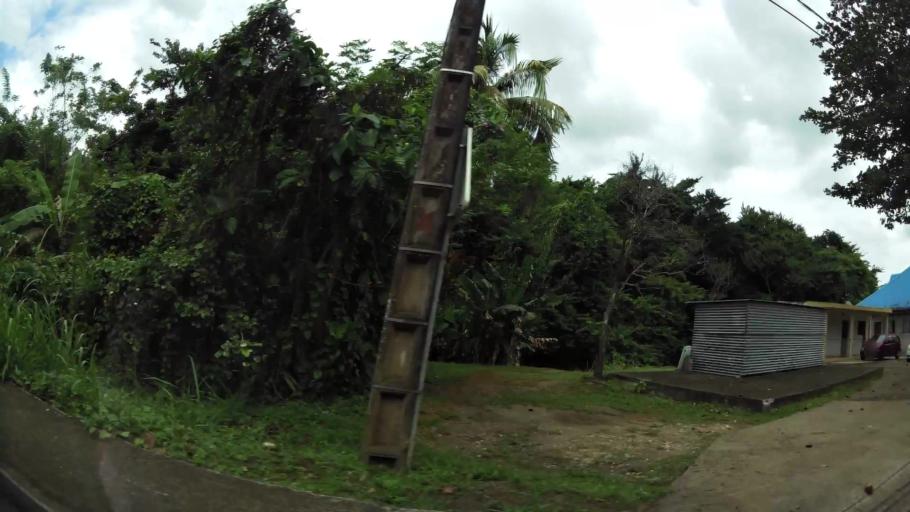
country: GP
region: Guadeloupe
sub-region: Guadeloupe
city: Lamentin
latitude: 16.2638
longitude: -61.6282
